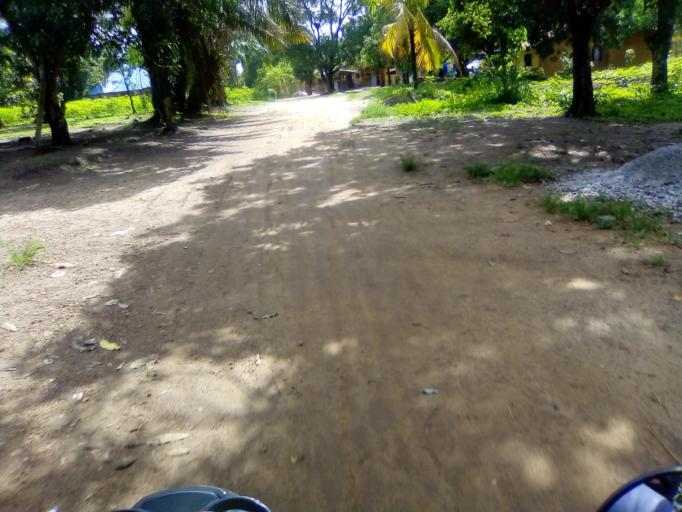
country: SL
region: Southern Province
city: Baoma
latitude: 7.9818
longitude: -11.7249
